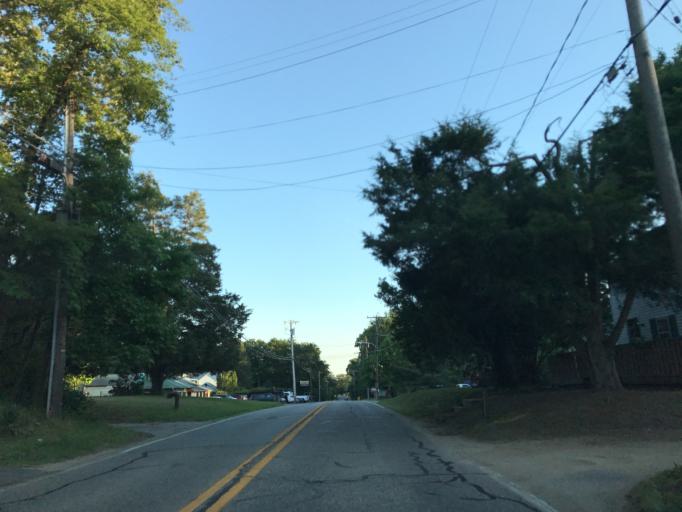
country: US
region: Maryland
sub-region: Anne Arundel County
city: Mayo
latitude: 38.8918
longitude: -76.5105
